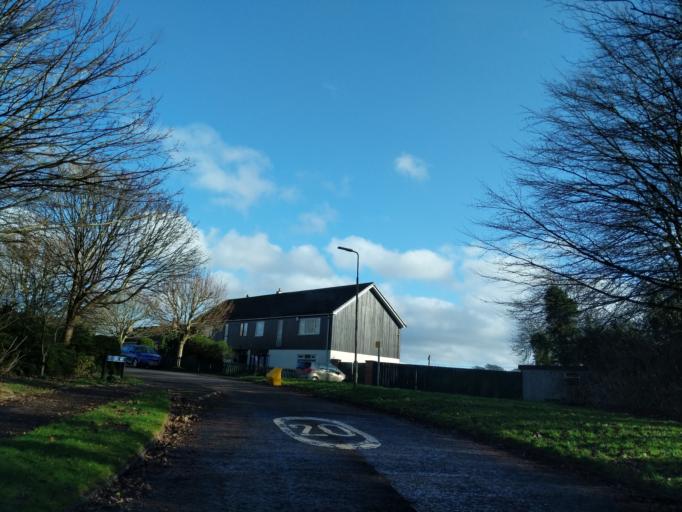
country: GB
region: Scotland
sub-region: West Lothian
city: Kirknewton
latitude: 55.8880
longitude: -3.4212
